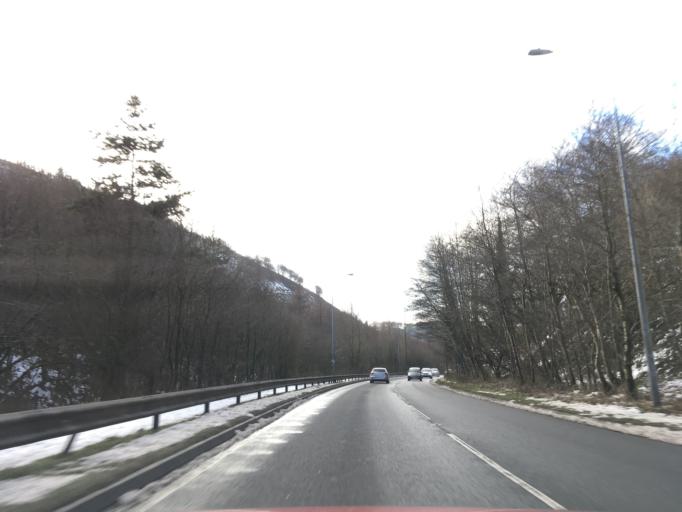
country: GB
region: Wales
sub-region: Torfaen County Borough
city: Pontypool
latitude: 51.6896
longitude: -3.0817
